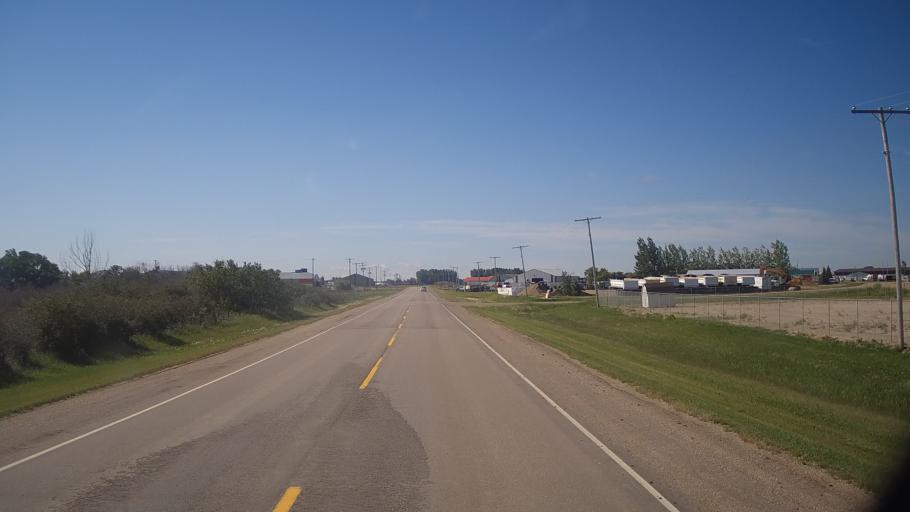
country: CA
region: Saskatchewan
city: Watrous
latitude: 51.6730
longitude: -105.4518
